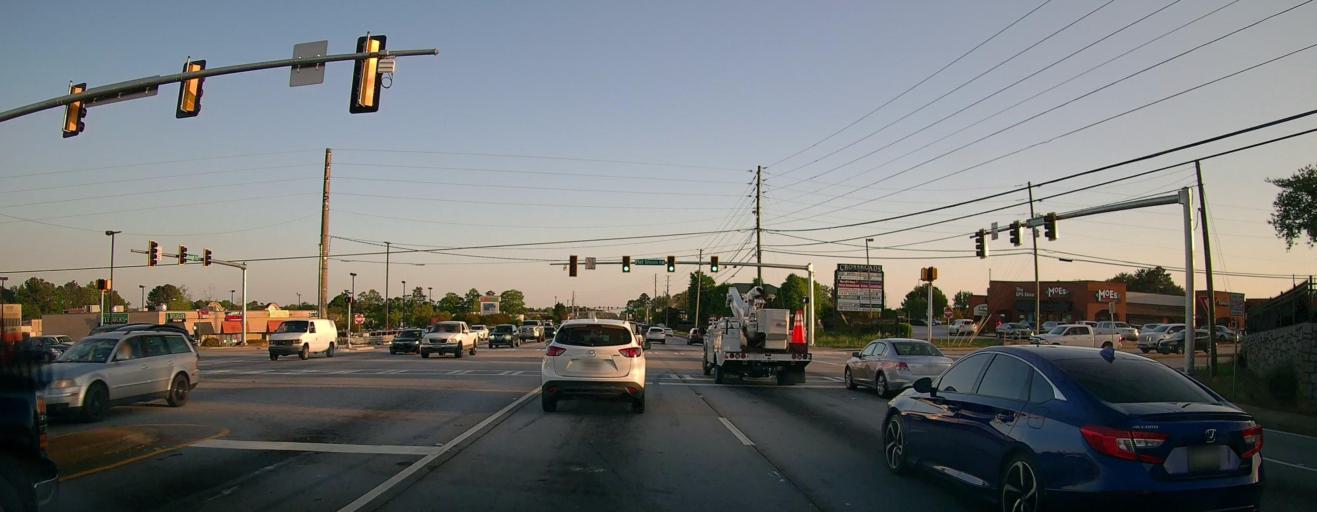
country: US
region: Georgia
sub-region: Rockdale County
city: Conyers
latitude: 33.6432
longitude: -84.0144
